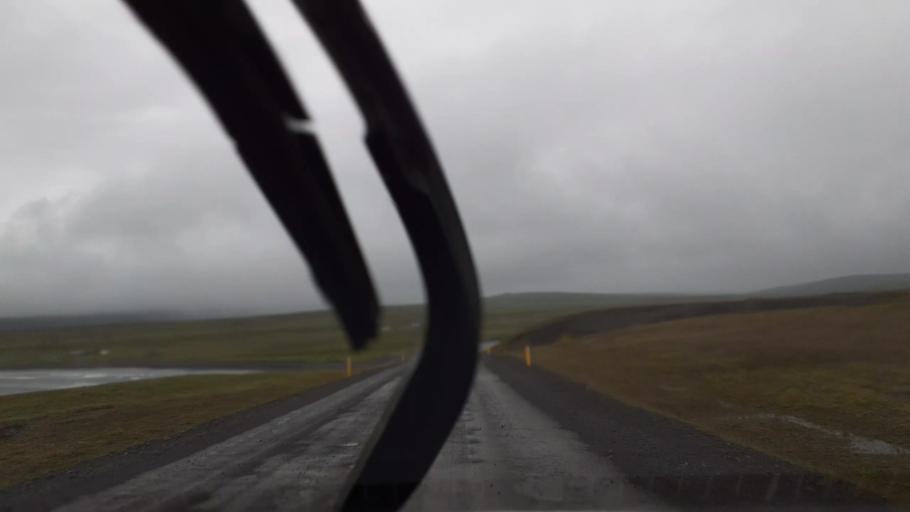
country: IS
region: East
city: Egilsstadir
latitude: 66.0469
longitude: -15.0944
